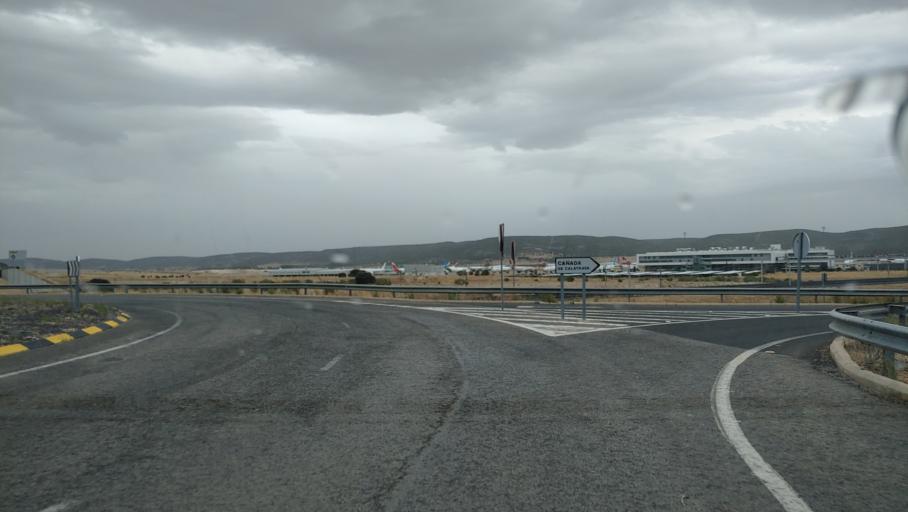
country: ES
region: Castille-La Mancha
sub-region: Provincia de Ciudad Real
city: Canada de Calatrava
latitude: 38.8734
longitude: -3.9930
